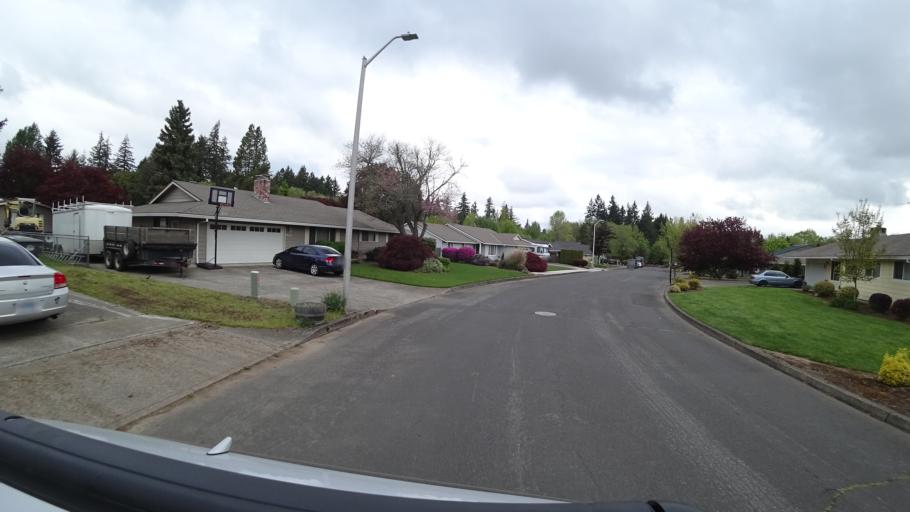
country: US
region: Oregon
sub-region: Washington County
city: Hillsboro
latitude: 45.5312
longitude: -122.9822
